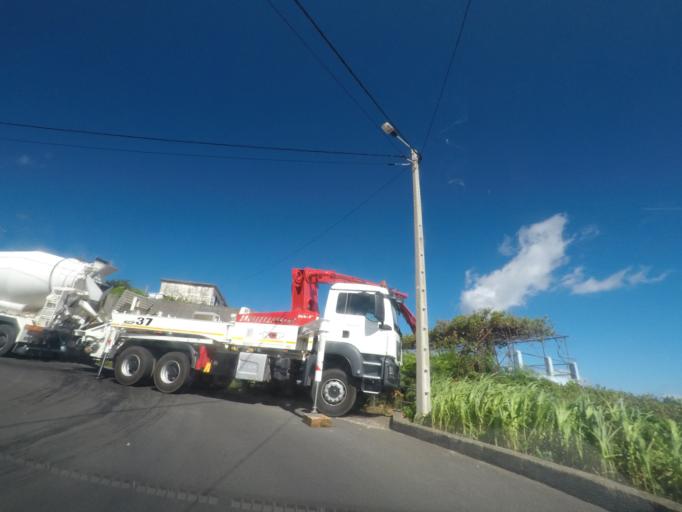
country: PT
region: Madeira
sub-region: Ribeira Brava
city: Campanario
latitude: 32.6978
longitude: -17.0251
